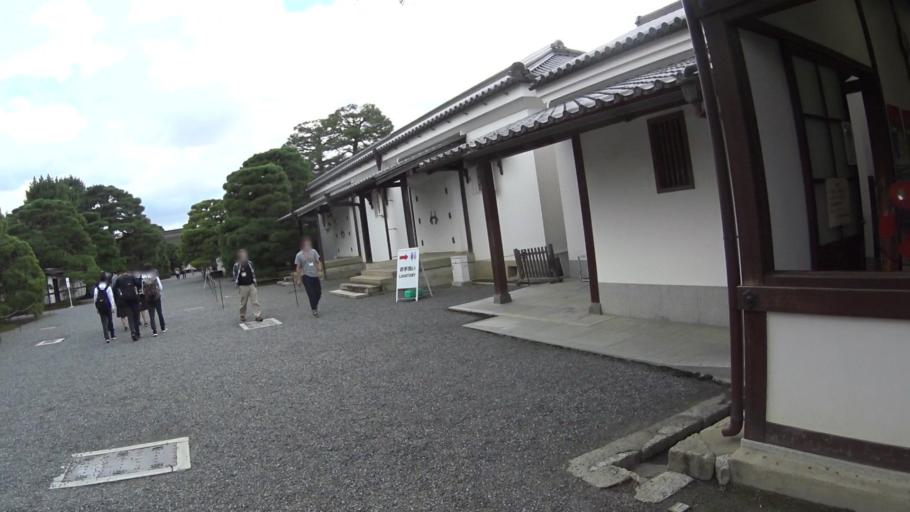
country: JP
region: Kyoto
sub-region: Kyoto-shi
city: Kamigyo-ku
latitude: 35.0254
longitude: 135.7612
